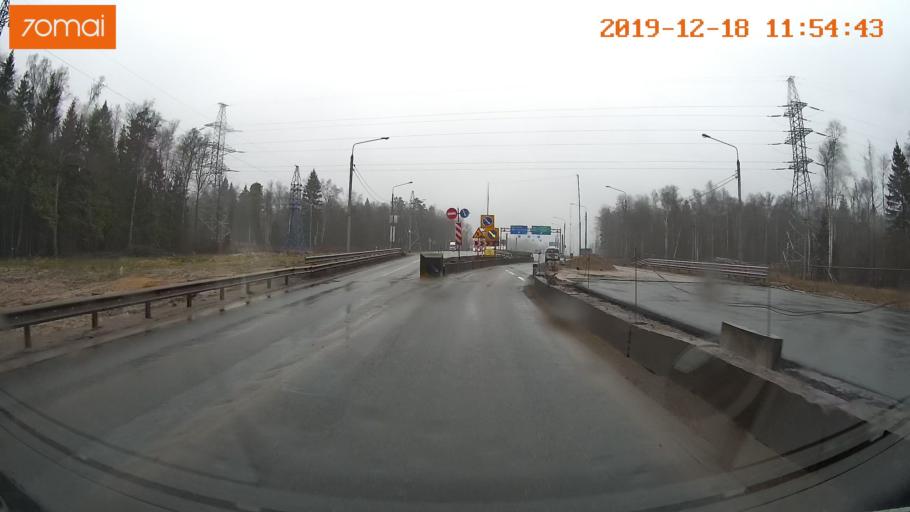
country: RU
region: Moskovskaya
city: Yershovo
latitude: 55.8183
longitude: 36.9175
